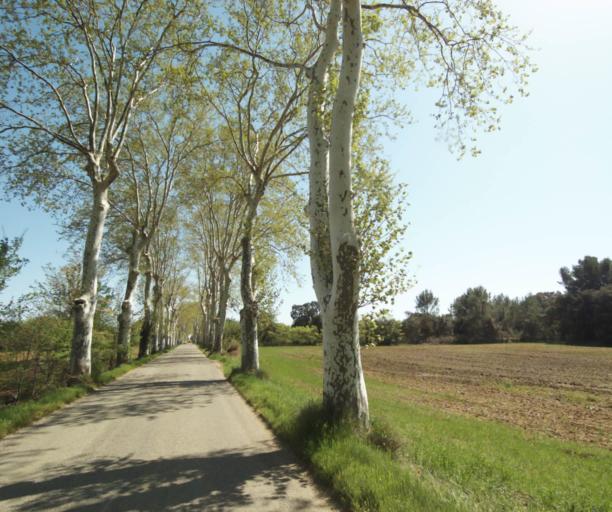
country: FR
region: Languedoc-Roussillon
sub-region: Departement de l'Herault
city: Saint-Drezery
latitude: 43.7255
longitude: 3.9850
